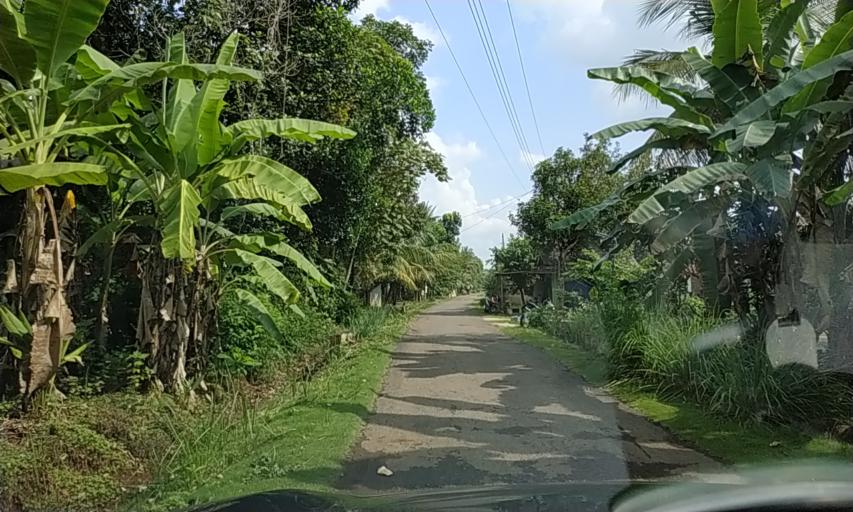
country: ID
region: Central Java
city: Bakung
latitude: -7.3424
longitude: 108.6678
